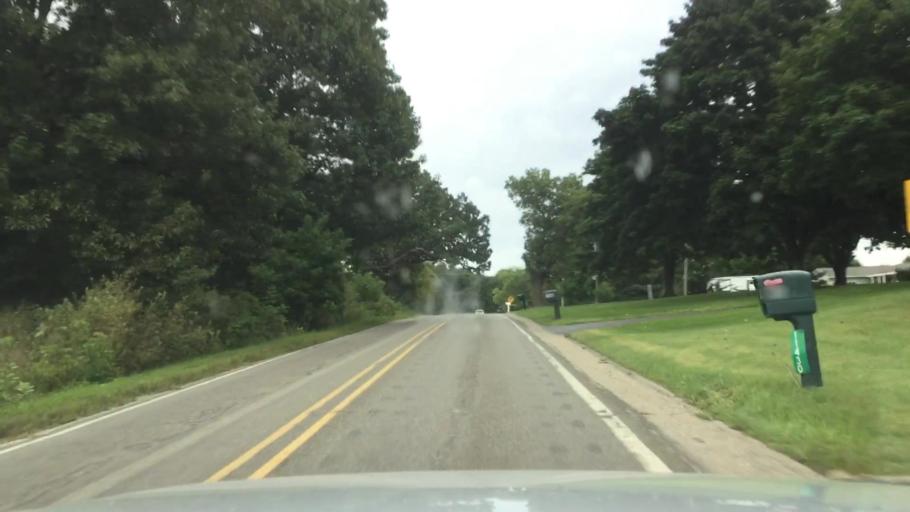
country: US
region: Michigan
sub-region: Genesee County
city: Argentine
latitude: 42.8171
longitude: -83.9317
